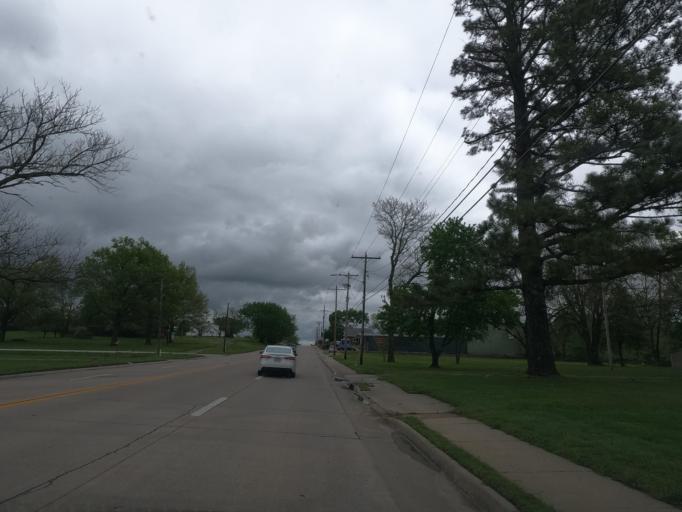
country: US
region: Kansas
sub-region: Labette County
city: Parsons
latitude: 37.3404
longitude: -95.2451
